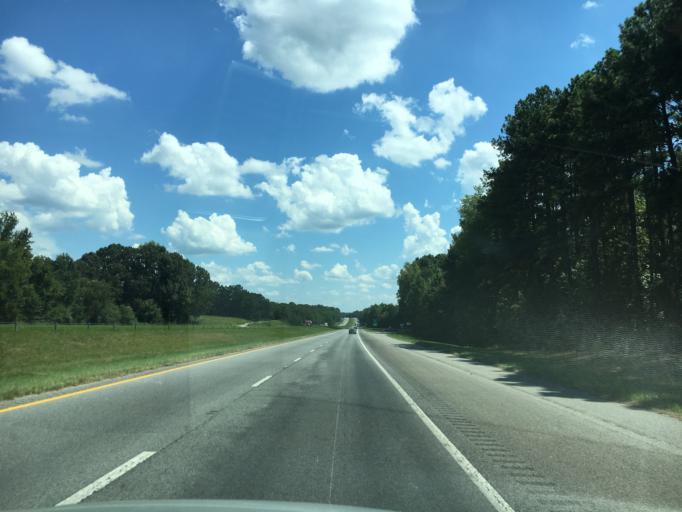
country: US
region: South Carolina
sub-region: Laurens County
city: Watts Mills
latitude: 34.6374
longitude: -81.9115
